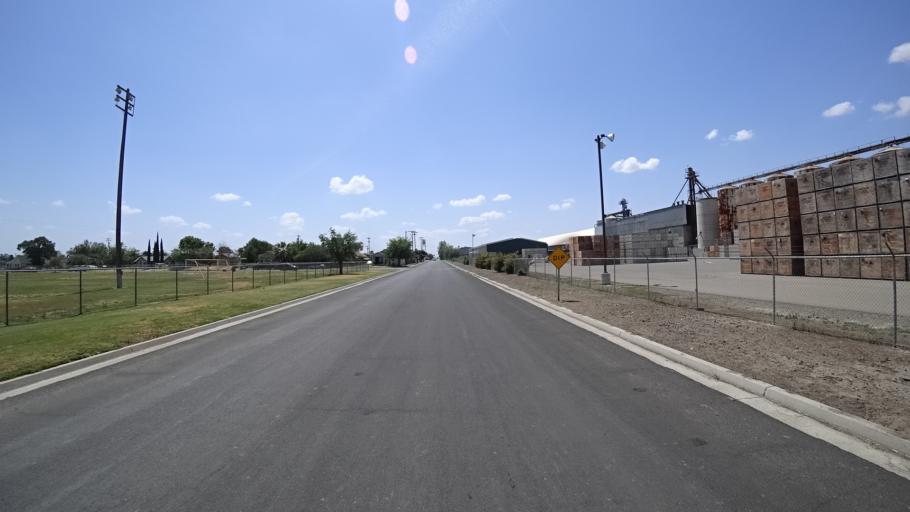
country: US
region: California
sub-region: Kings County
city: Stratford
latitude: 36.1924
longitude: -119.8245
